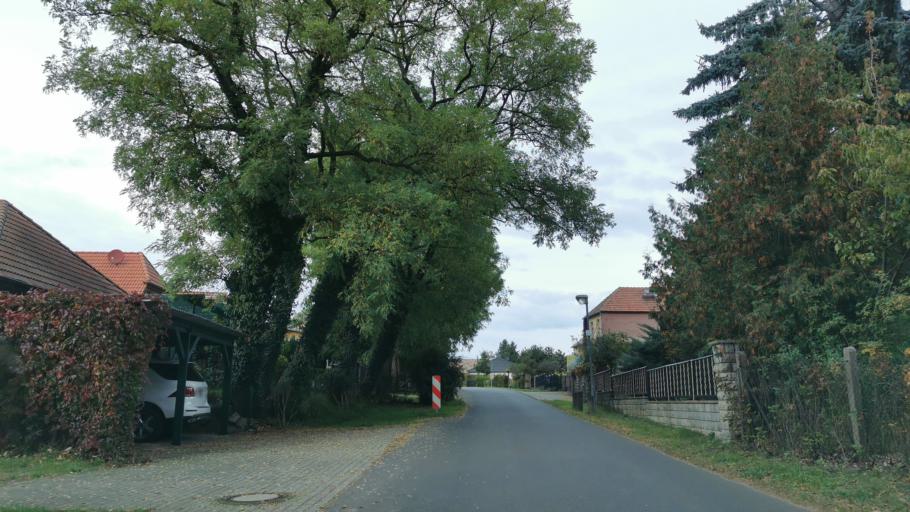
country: DE
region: Brandenburg
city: Werder
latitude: 52.3527
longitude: 12.9489
